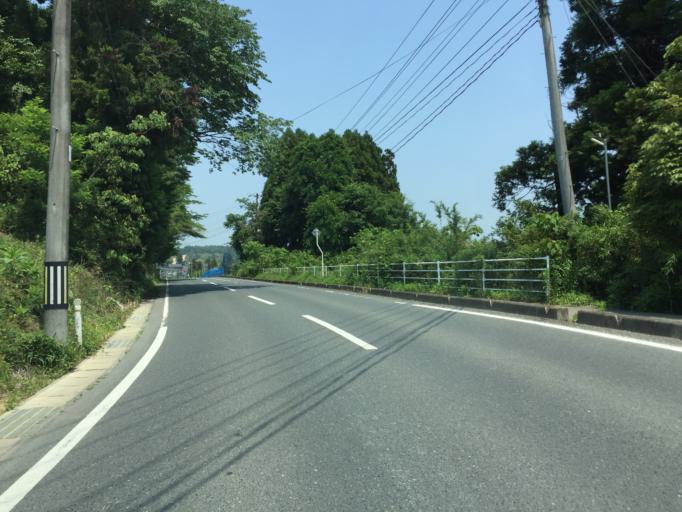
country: JP
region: Miyagi
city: Marumori
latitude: 37.8258
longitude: 140.8958
